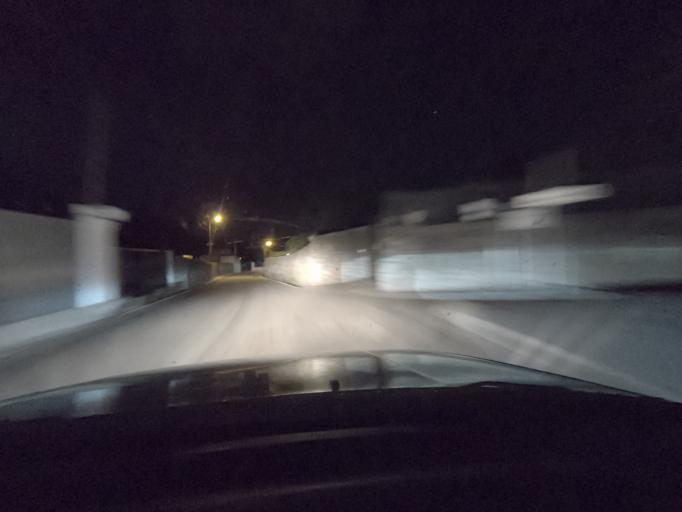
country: PT
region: Vila Real
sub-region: Peso da Regua
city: Godim
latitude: 41.1888
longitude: -7.7923
